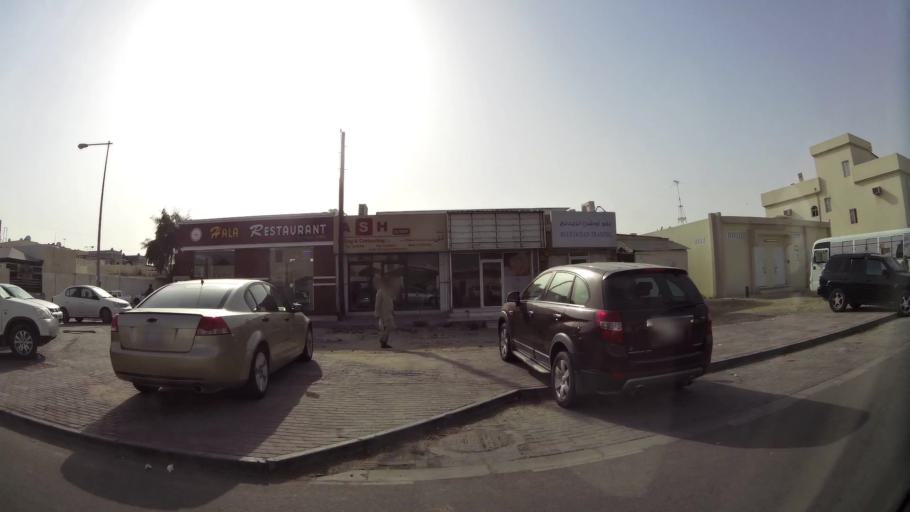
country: QA
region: Baladiyat ar Rayyan
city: Ar Rayyan
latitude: 25.2378
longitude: 51.4344
